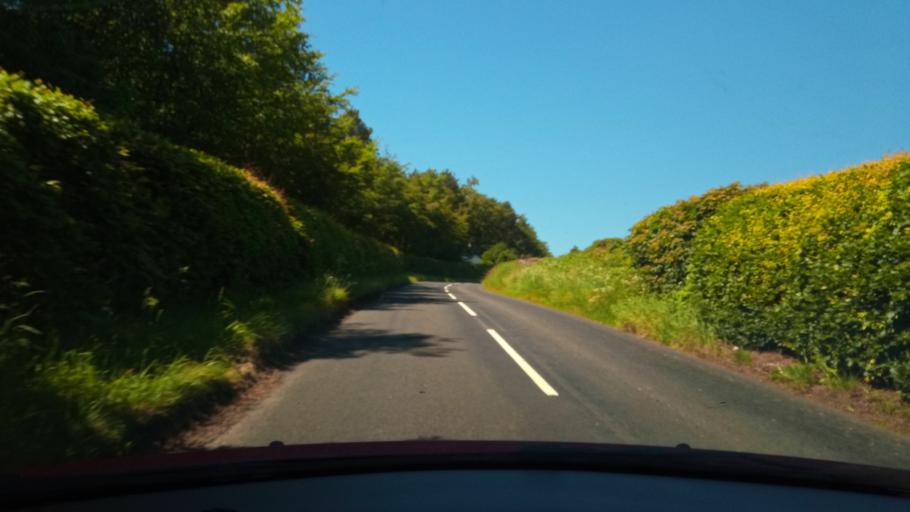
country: GB
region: Scotland
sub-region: The Scottish Borders
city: Duns
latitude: 55.7772
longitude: -2.4068
